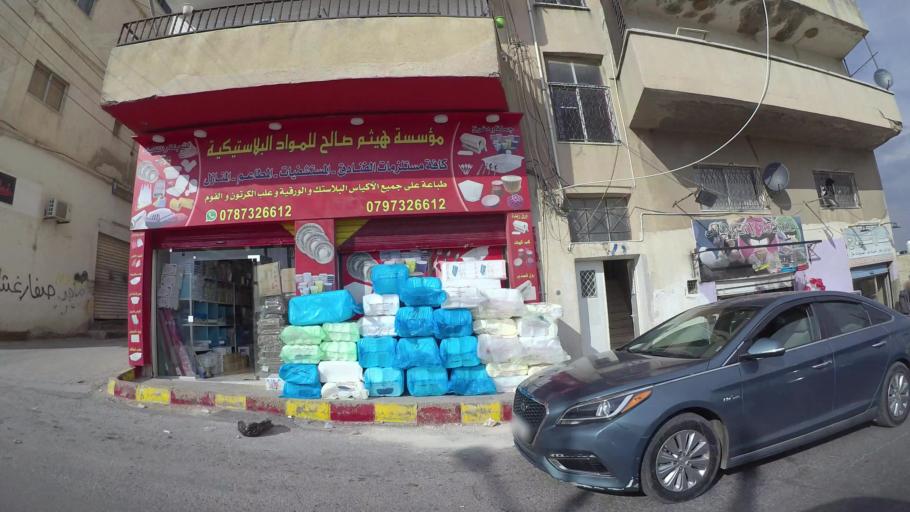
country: JO
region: Amman
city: Amman
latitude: 31.9987
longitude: 35.9466
